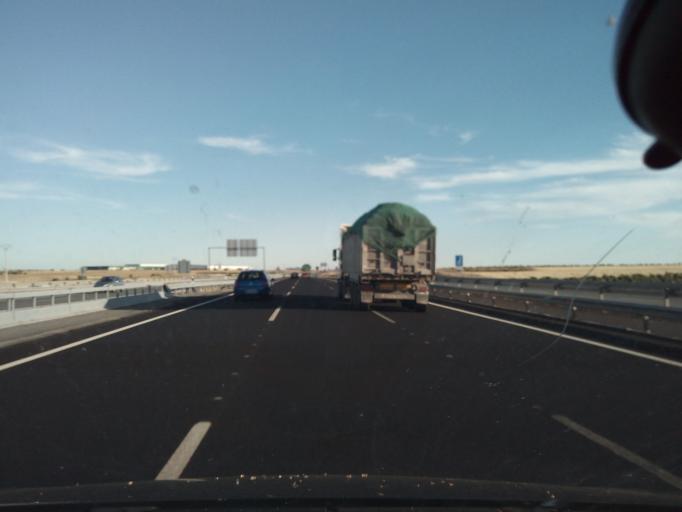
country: ES
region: Castille-La Mancha
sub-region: Province of Toledo
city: Dosbarrios
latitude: 39.9053
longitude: -3.4745
